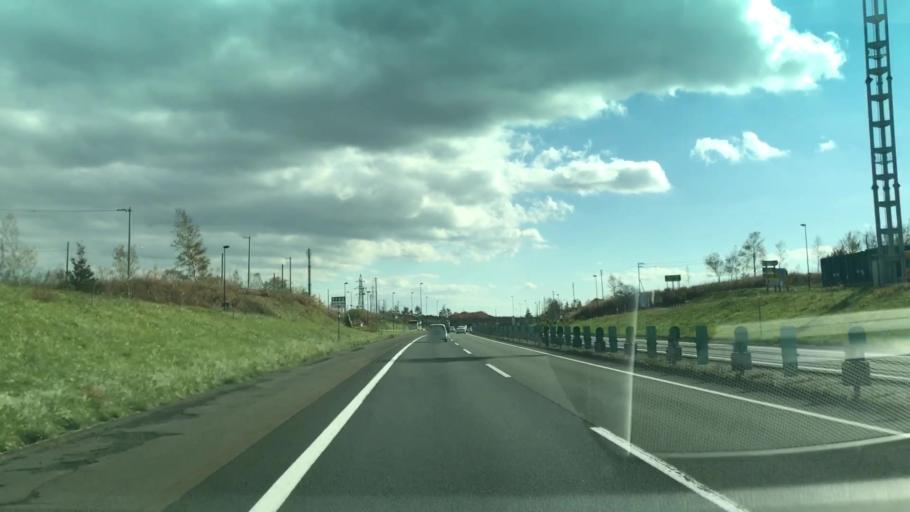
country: JP
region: Hokkaido
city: Kitahiroshima
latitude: 42.9516
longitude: 141.5120
